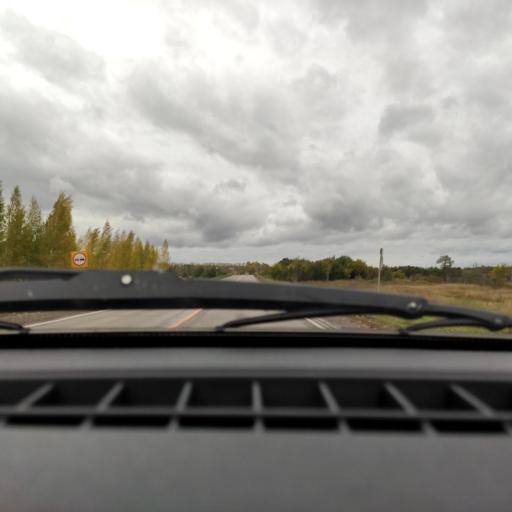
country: RU
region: Bashkortostan
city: Chishmy
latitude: 54.4394
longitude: 55.2389
